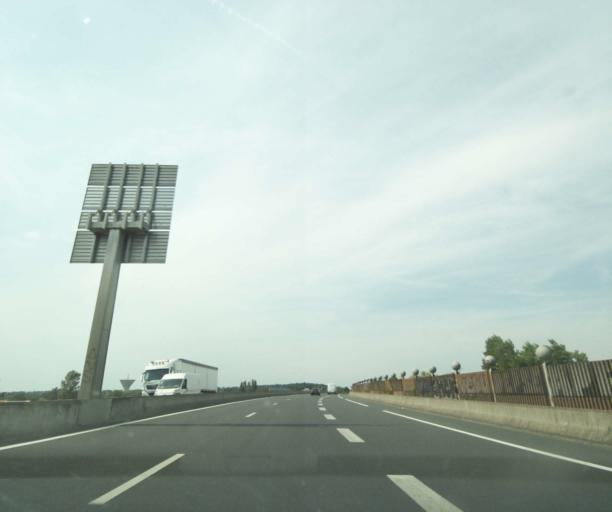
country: FR
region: Centre
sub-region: Departement d'Indre-et-Loire
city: La Riche
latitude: 47.3782
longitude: 0.6497
